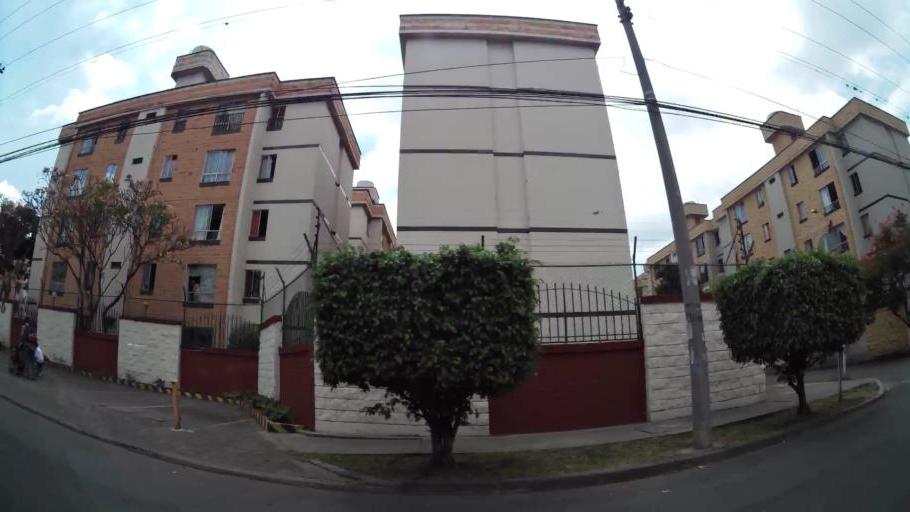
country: CO
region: Valle del Cauca
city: Cali
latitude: 3.4724
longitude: -76.5004
